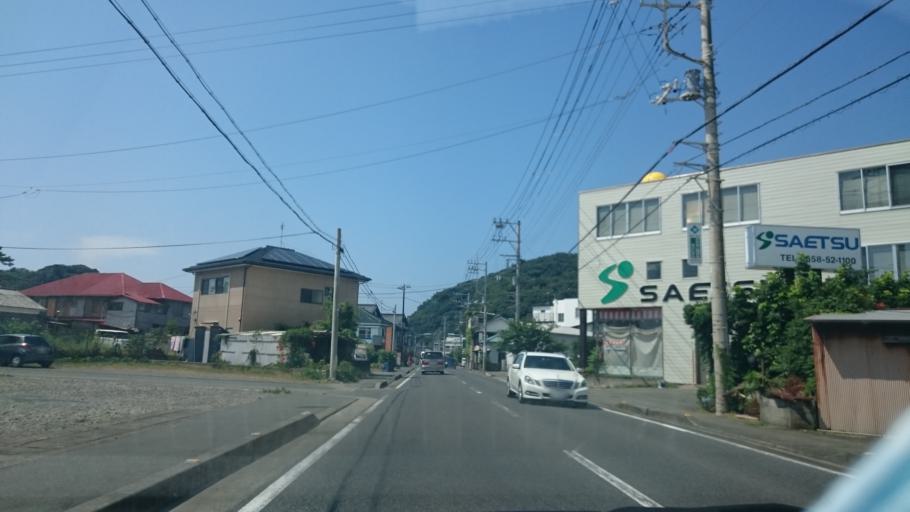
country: JP
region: Shizuoka
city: Heda
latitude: 34.7688
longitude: 138.7769
